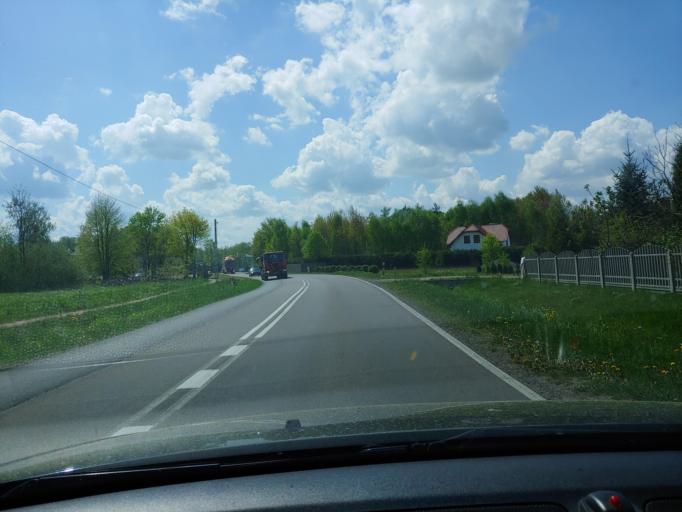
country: PL
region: Subcarpathian Voivodeship
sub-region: Powiat mielecki
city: Wadowice Gorne
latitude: 50.2568
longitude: 21.3255
